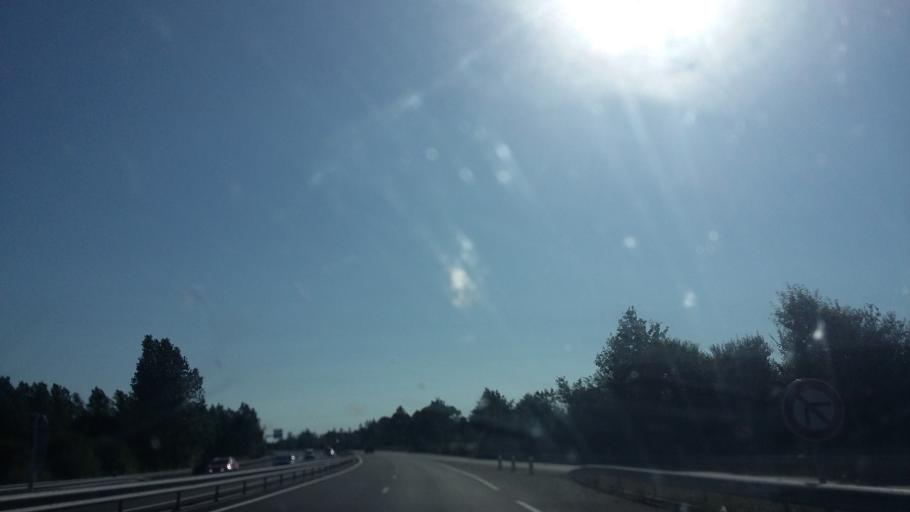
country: FR
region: Pays de la Loire
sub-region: Departement de la Vendee
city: Challans
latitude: 46.8547
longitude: -1.9000
